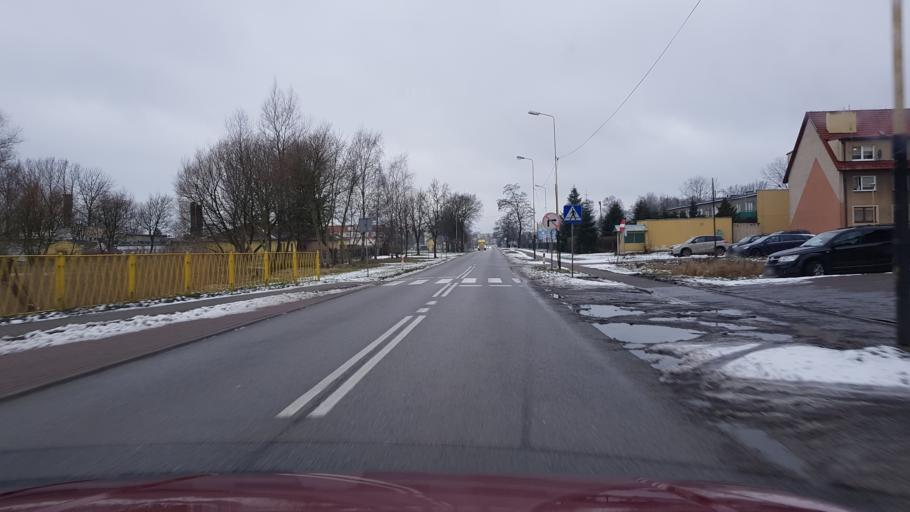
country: PL
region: West Pomeranian Voivodeship
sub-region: Powiat goleniowski
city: Nowogard
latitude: 53.6637
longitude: 15.1486
